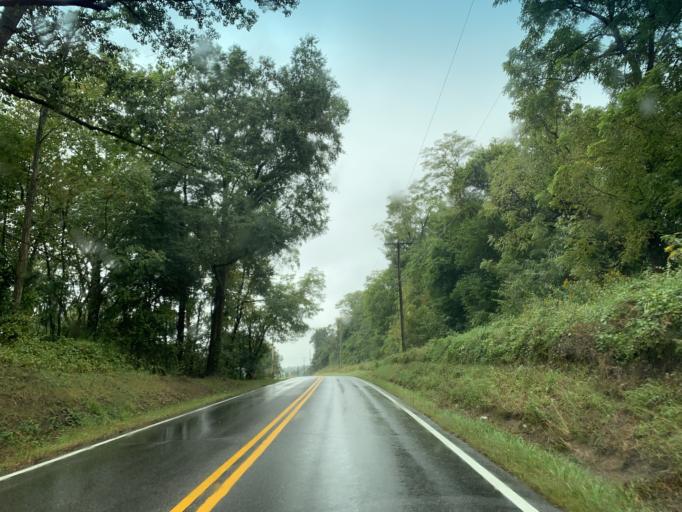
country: US
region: Maryland
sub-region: Queen Anne's County
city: Kingstown
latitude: 39.2623
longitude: -75.8555
